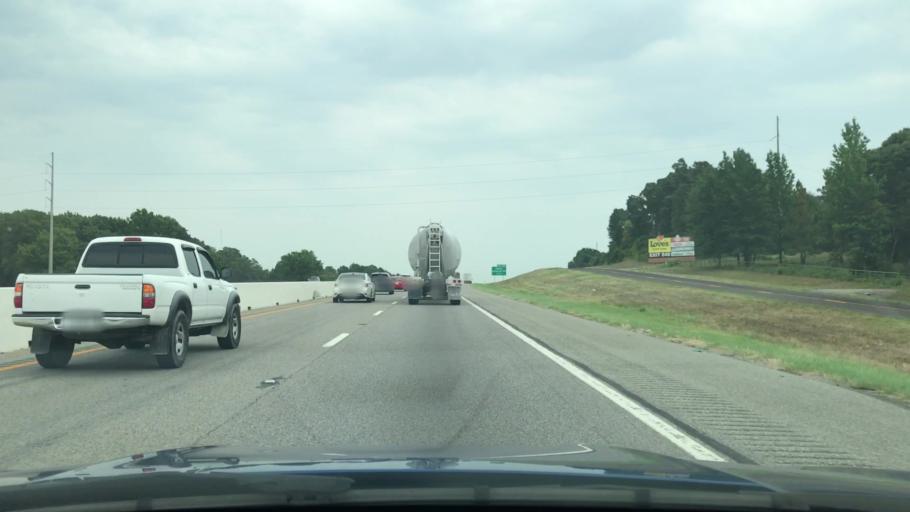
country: US
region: Texas
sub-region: Van Zandt County
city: Canton
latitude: 32.5511
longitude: -95.7809
